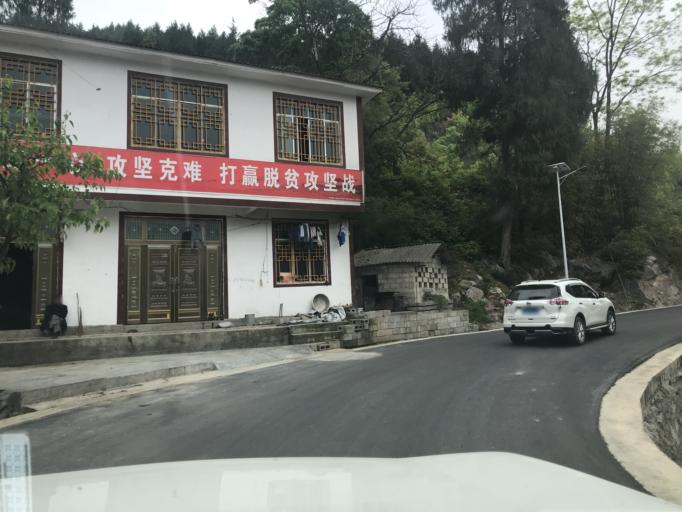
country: CN
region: Guizhou Sheng
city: Tongjing
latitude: 28.3065
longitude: 108.2669
